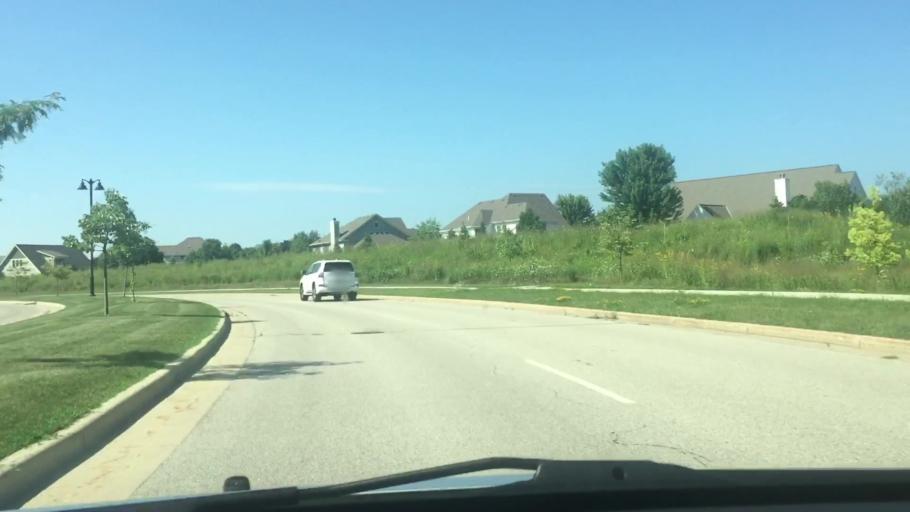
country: US
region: Wisconsin
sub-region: Waukesha County
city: Delafield
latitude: 43.0705
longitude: -88.4575
